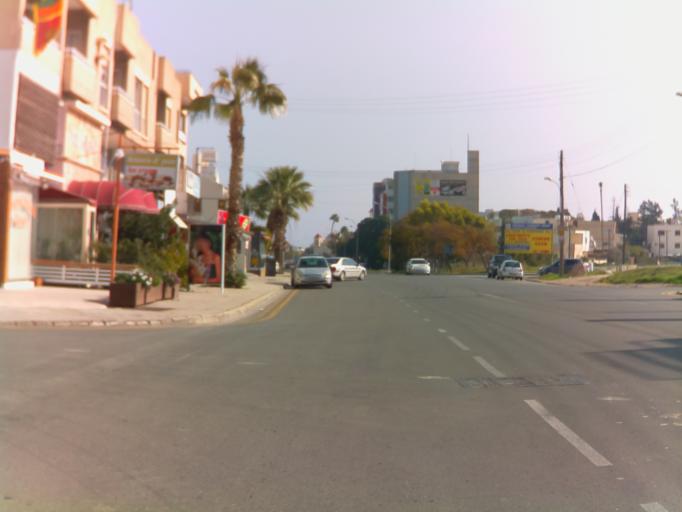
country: CY
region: Larnaka
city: Larnaca
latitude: 34.9111
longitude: 33.6226
